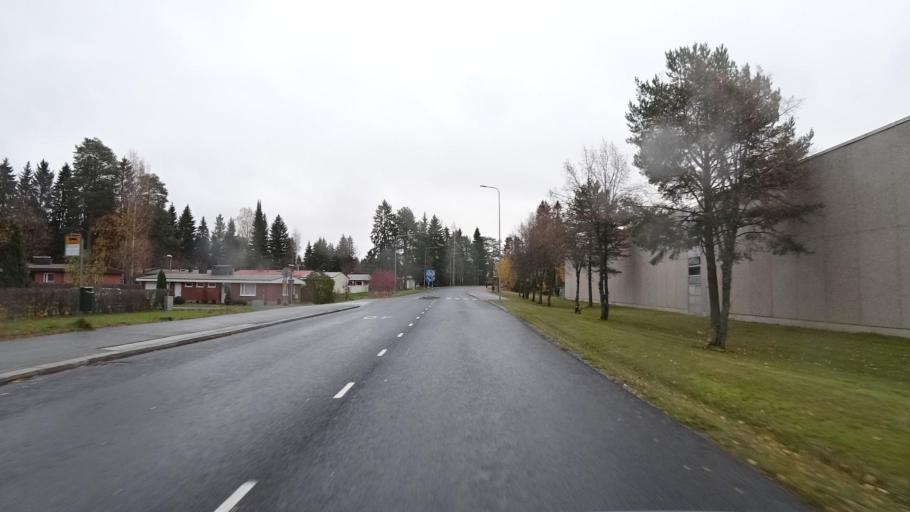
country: FI
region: Northern Savo
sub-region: Kuopio
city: Kuopio
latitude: 62.9302
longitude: 27.6854
